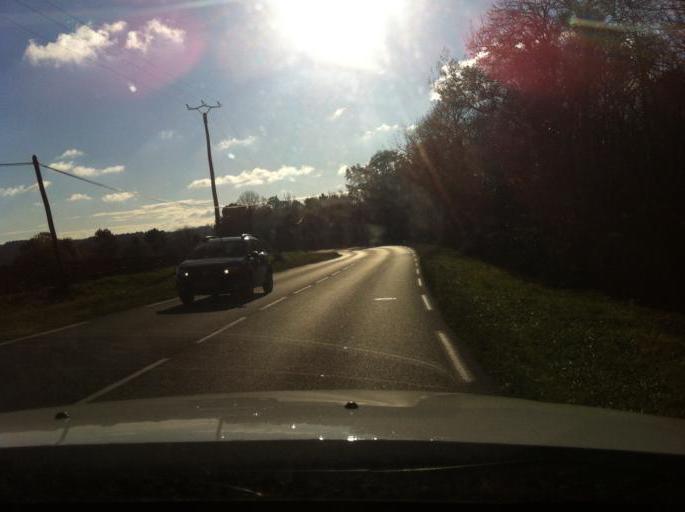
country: FR
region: Aquitaine
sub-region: Departement de la Dordogne
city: Rouffignac-Saint-Cernin-de-Reilhac
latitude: 45.0508
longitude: 0.8598
